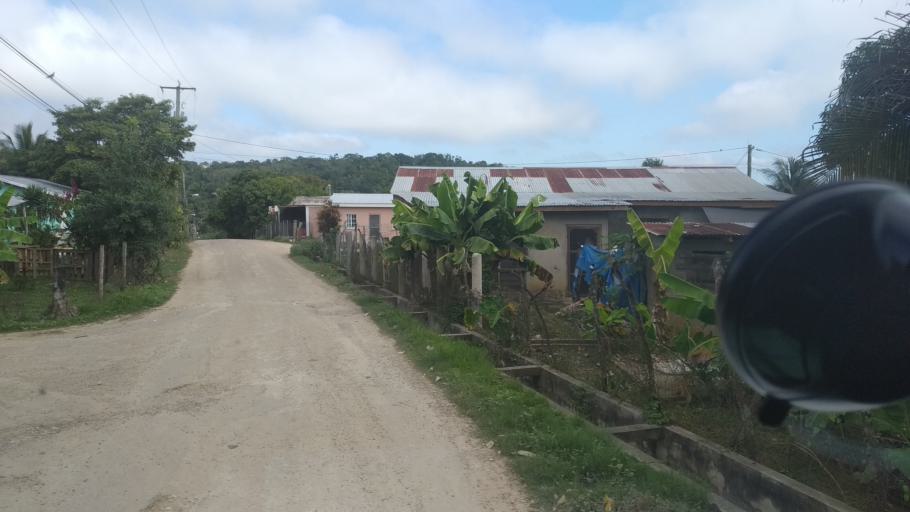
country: BZ
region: Cayo
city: Benque Viejo del Carmen
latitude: 17.0836
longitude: -89.1305
